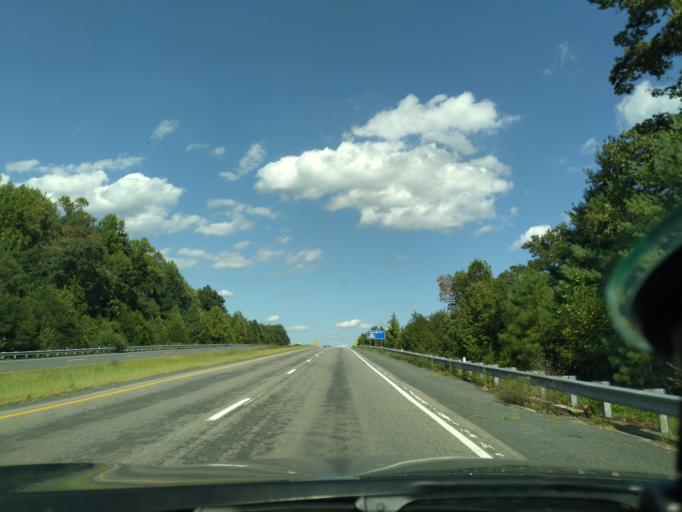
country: US
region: Virginia
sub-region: Caroline County
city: Bowling Green
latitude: 38.0393
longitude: -77.3473
